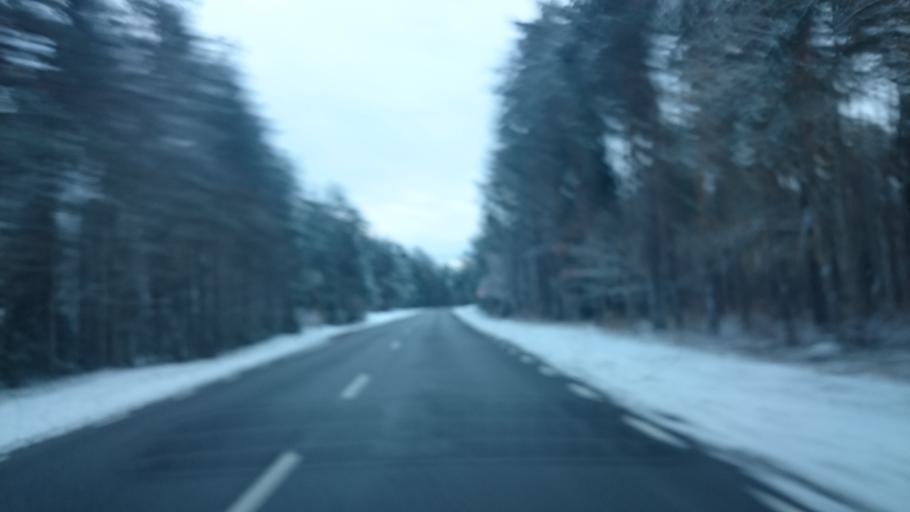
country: EE
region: Saare
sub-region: Kuressaare linn
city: Kuressaare
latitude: 58.3917
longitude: 22.6482
